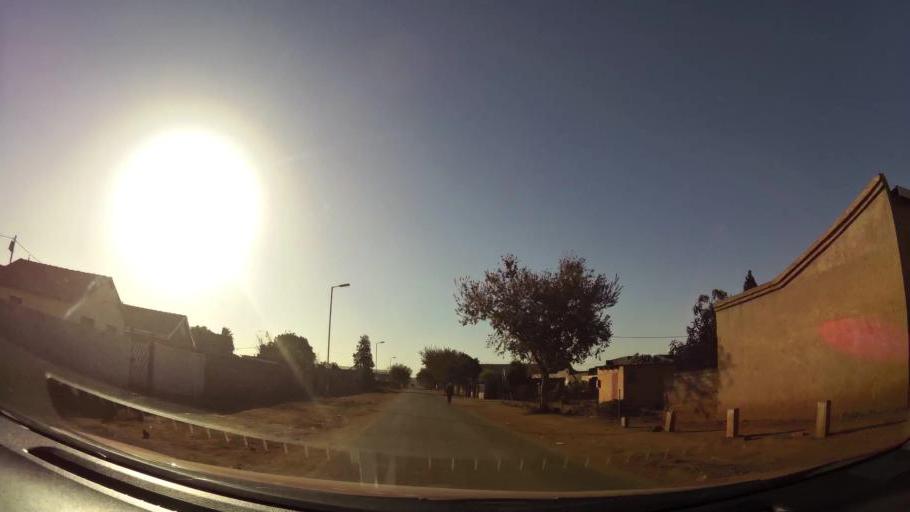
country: ZA
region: Gauteng
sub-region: City of Tshwane Metropolitan Municipality
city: Mabopane
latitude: -25.5913
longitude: 28.1011
